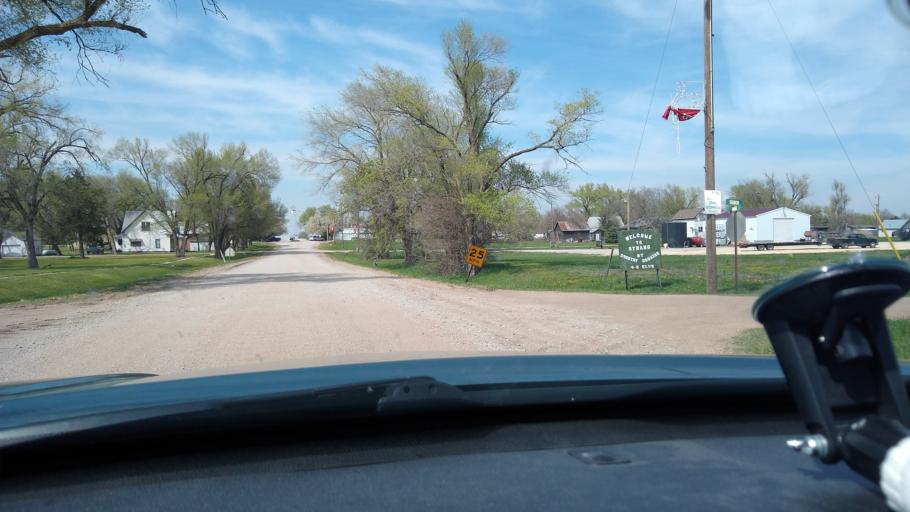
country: US
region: Nebraska
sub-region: Fillmore County
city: Geneva
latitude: 40.4124
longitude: -97.5868
